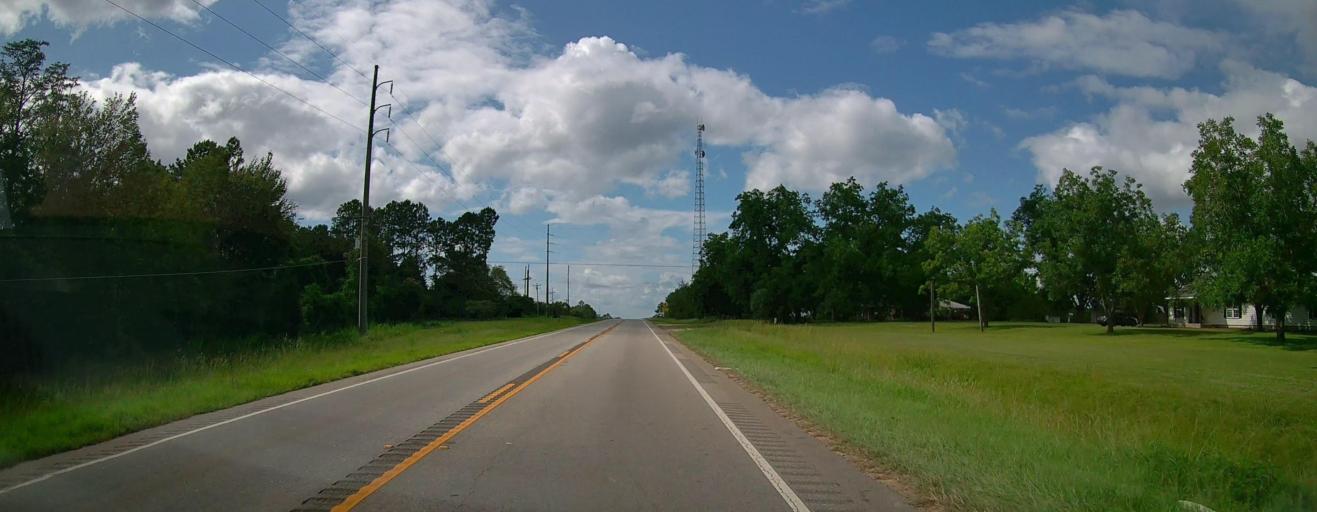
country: US
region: Georgia
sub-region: Coffee County
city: Douglas
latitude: 31.5275
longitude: -82.8772
